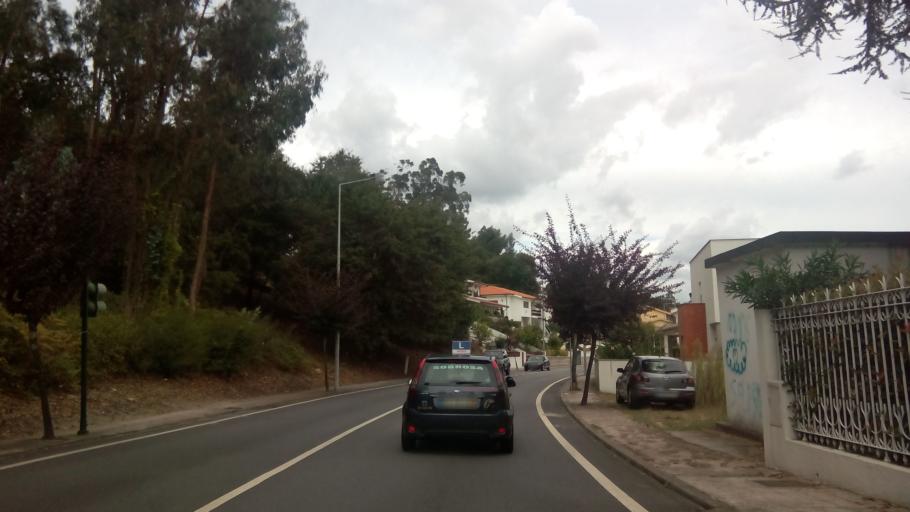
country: PT
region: Porto
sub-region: Paredes
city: Casteloes de Cepeda
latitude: 41.2057
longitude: -8.3420
